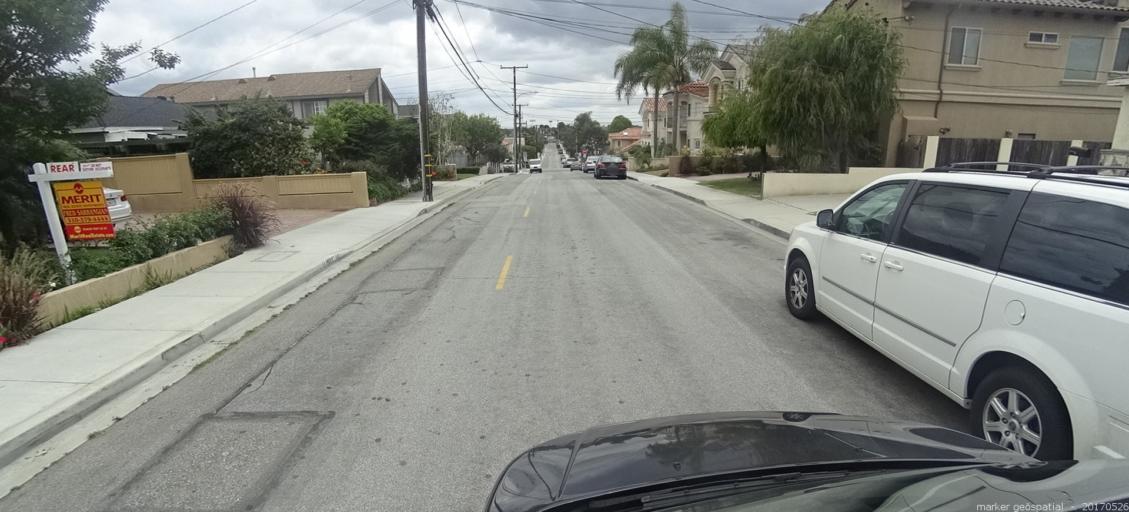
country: US
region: California
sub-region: Los Angeles County
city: Lawndale
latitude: 33.8819
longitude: -118.3781
